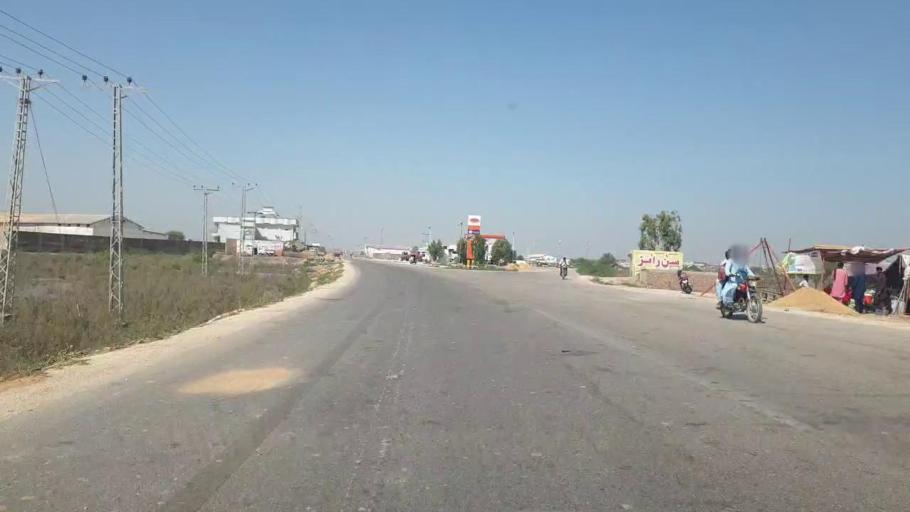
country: PK
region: Sindh
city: Talhar
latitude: 24.8734
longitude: 68.8164
